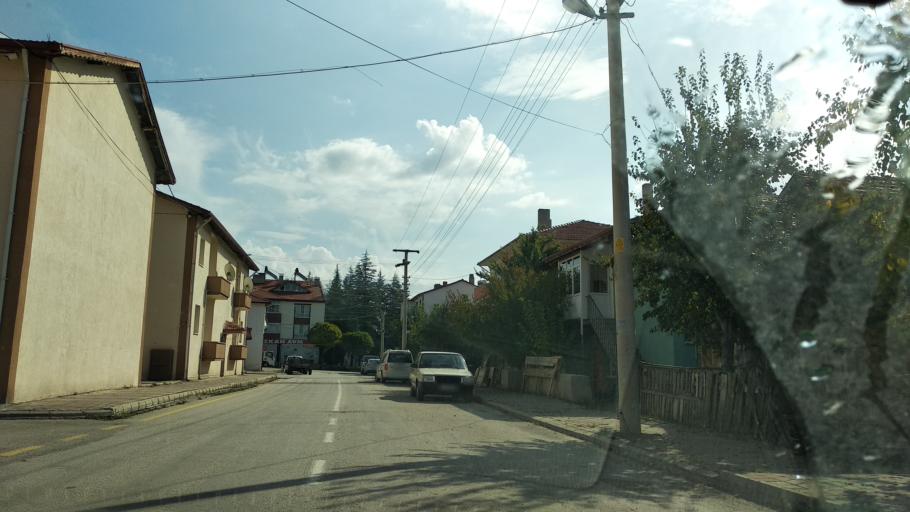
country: TR
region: Bolu
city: Seben
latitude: 40.4099
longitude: 31.5718
